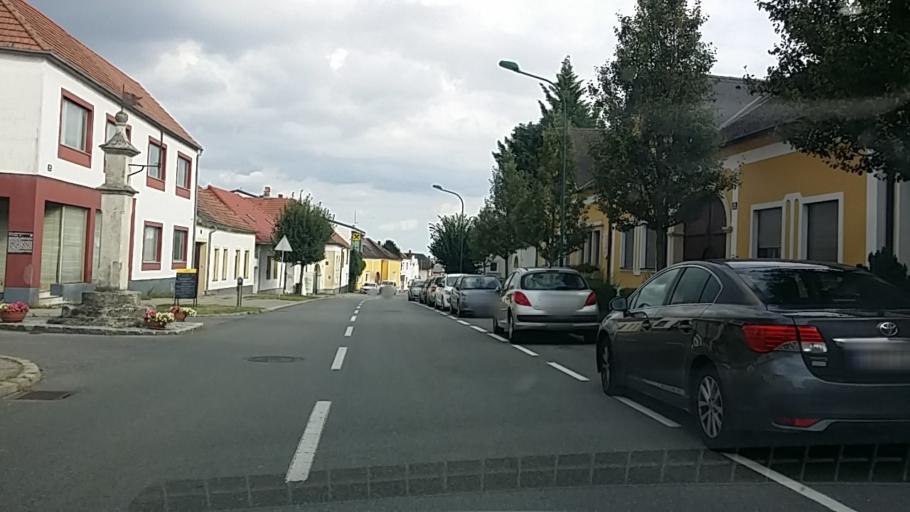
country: AT
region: Burgenland
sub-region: Eisenstadt-Umgebung
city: Donnerskirchen
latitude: 47.8971
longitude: 16.6427
